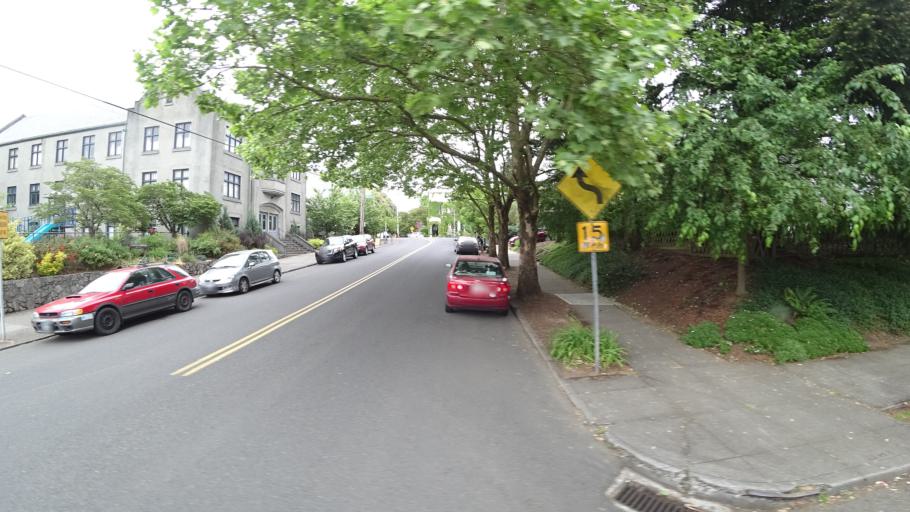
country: US
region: Oregon
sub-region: Multnomah County
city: Lents
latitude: 45.5165
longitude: -122.6079
